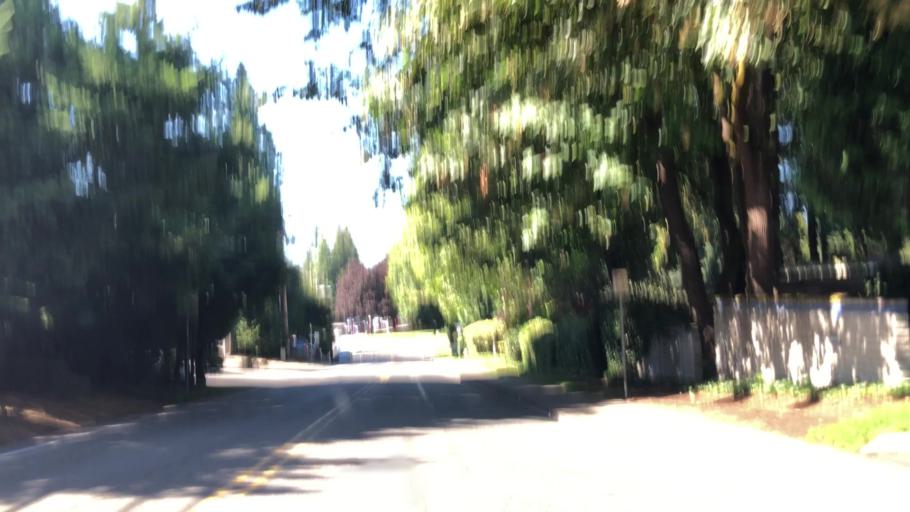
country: US
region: Washington
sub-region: King County
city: Inglewood-Finn Hill
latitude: 47.7085
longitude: -122.2079
